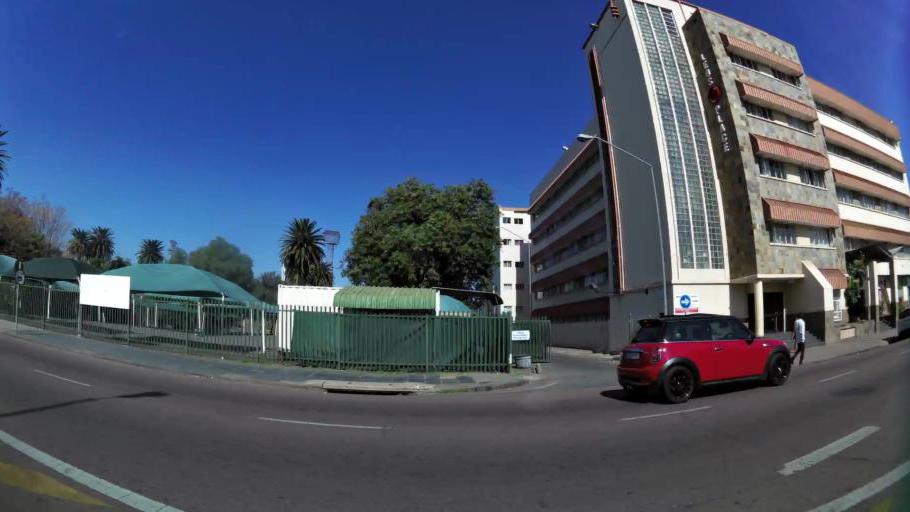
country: ZA
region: Gauteng
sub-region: City of Tshwane Metropolitan Municipality
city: Pretoria
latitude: -25.7454
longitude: 28.2008
